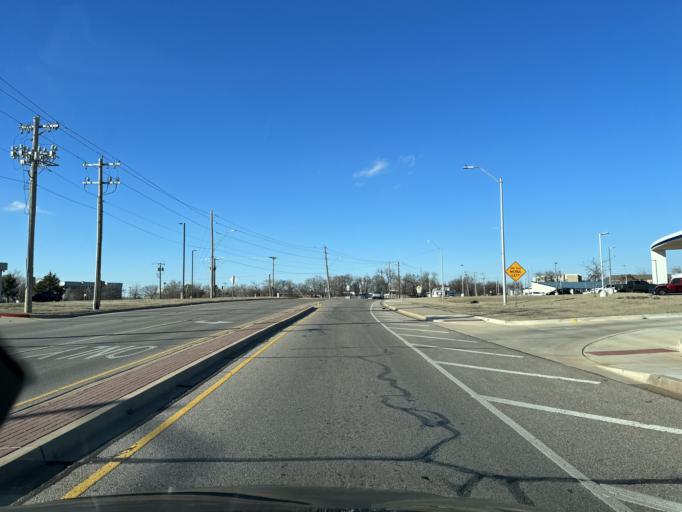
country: US
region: Oklahoma
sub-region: Oklahoma County
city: Midwest City
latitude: 35.4428
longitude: -97.4160
